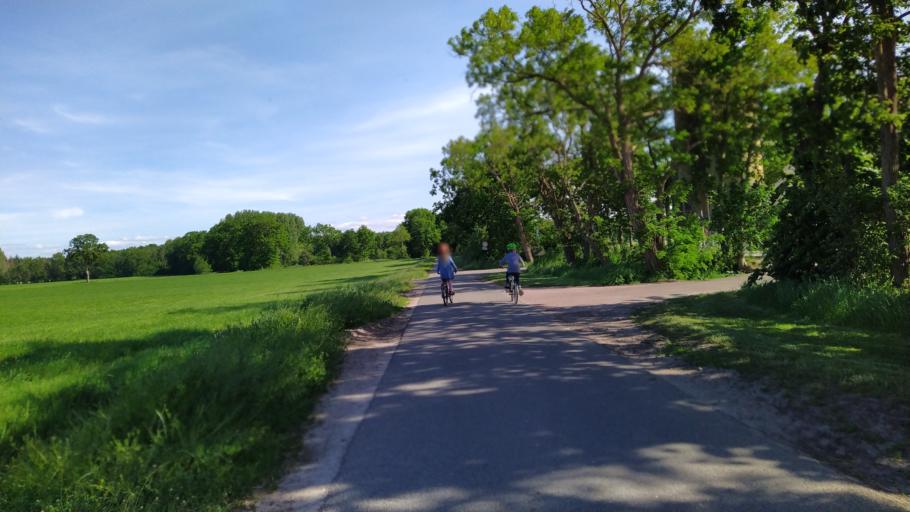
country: DE
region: Lower Saxony
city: Ahlerstedt
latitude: 53.4297
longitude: 9.4702
